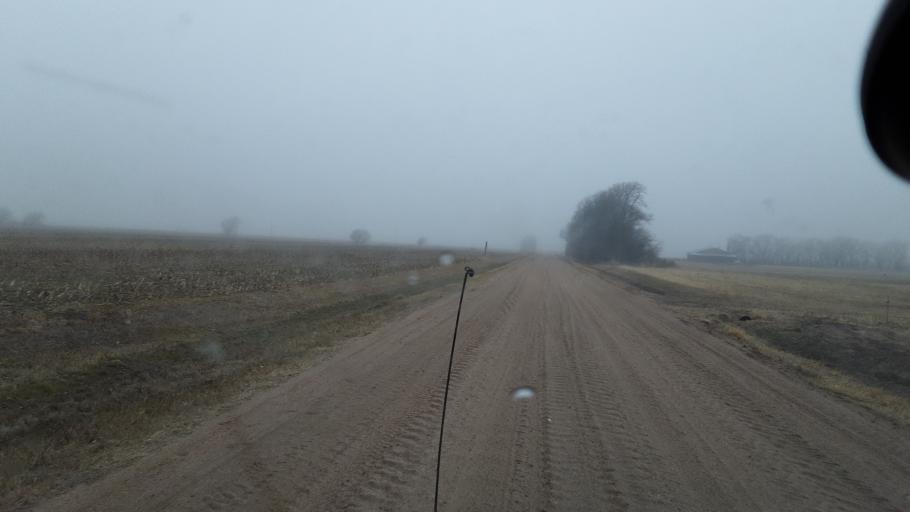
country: US
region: Kansas
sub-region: Reno County
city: South Hutchinson
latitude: 37.9553
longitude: -97.9542
